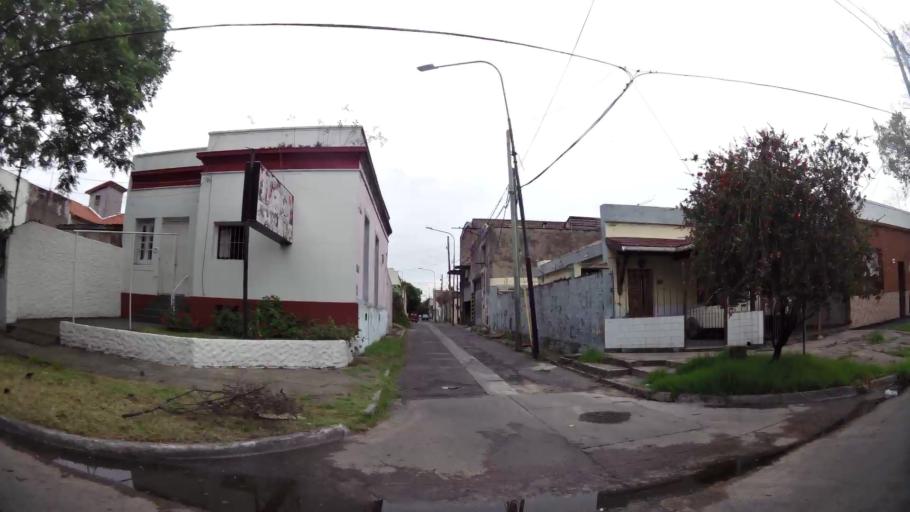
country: AR
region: Buenos Aires
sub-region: Partido de Lanus
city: Lanus
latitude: -34.6986
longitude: -58.3759
